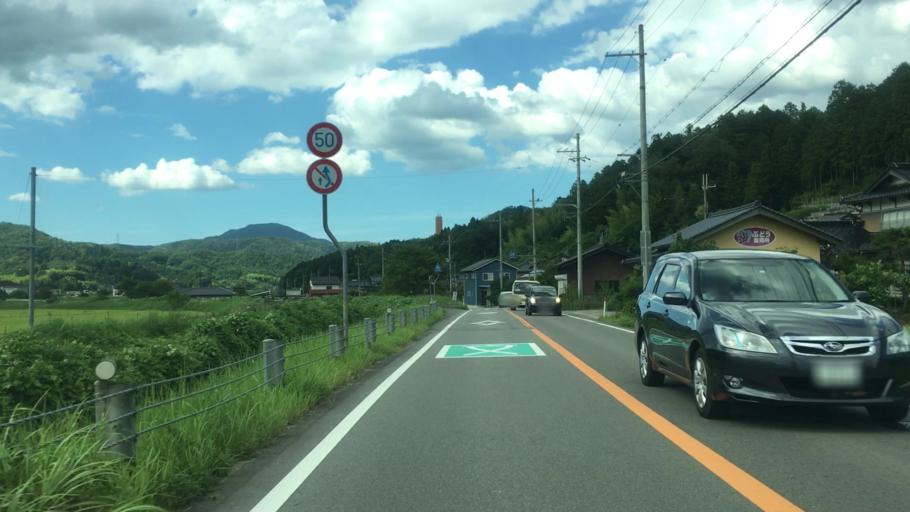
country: JP
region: Hyogo
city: Toyooka
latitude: 35.5393
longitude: 134.7900
